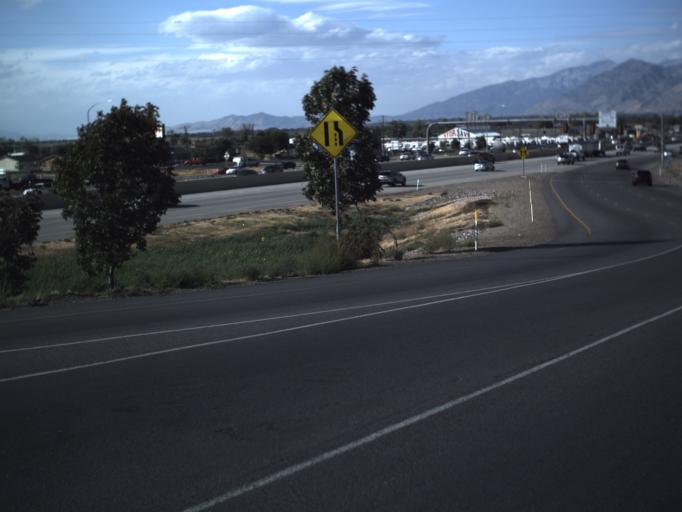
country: US
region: Utah
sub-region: Utah County
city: Springville
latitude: 40.1618
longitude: -111.6457
